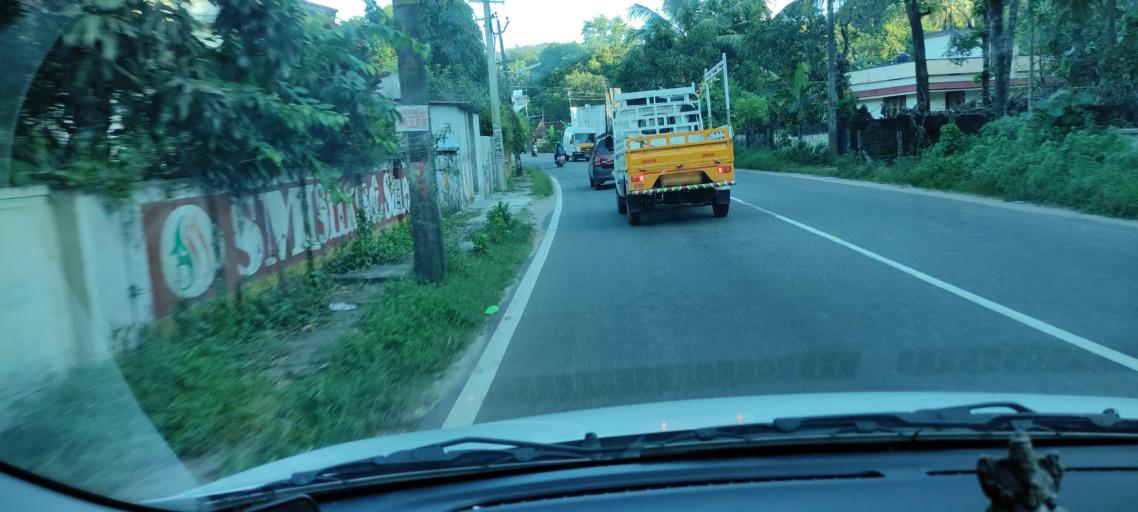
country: IN
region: Kerala
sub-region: Pattanamtitta
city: Adur
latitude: 9.1433
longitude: 76.7759
